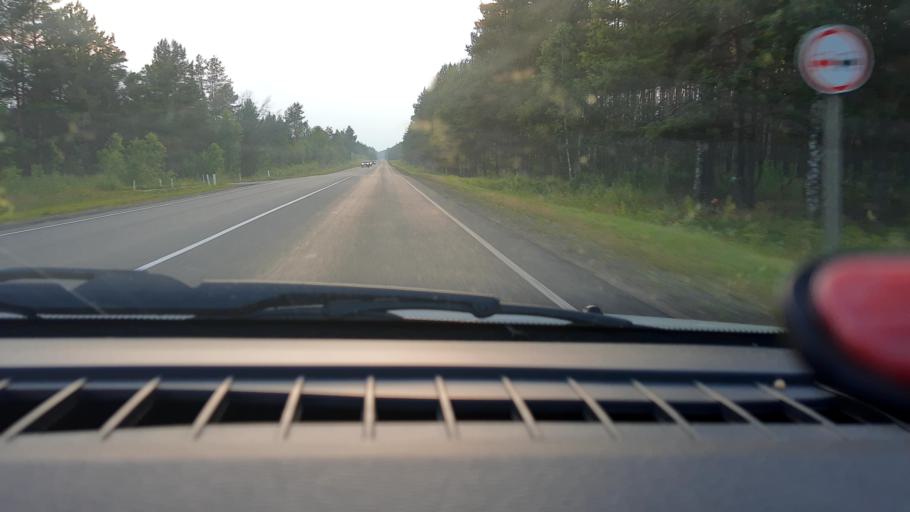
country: RU
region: Nizjnij Novgorod
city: Shatki
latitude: 55.1427
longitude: 44.2273
